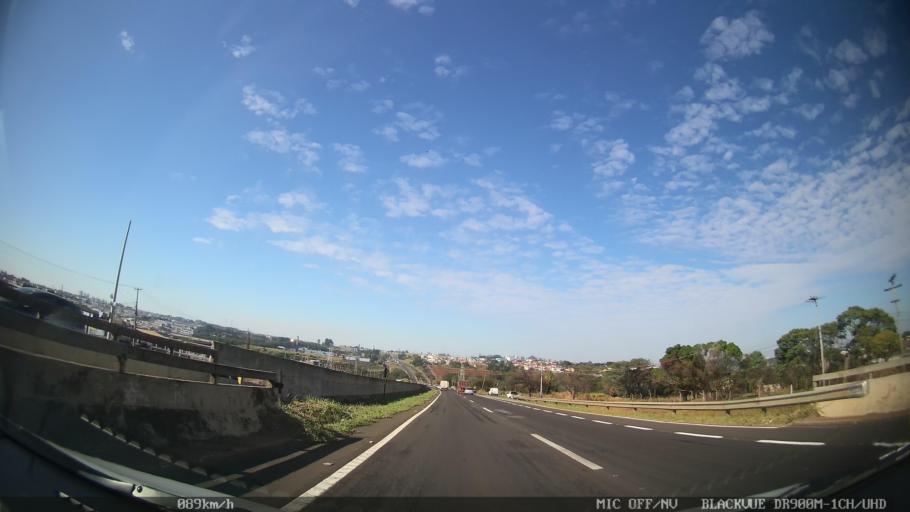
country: BR
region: Sao Paulo
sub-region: Americana
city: Americana
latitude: -22.7592
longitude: -47.3190
